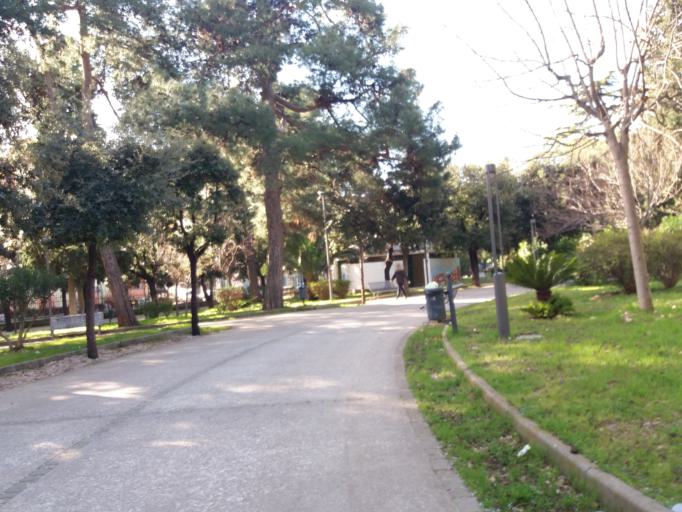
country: IT
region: Apulia
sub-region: Provincia di Bari
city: Bitonto
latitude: 41.1123
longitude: 16.6969
